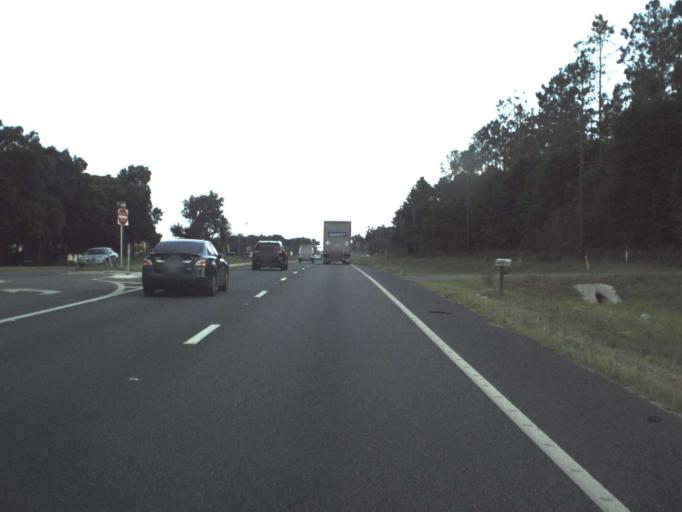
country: US
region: Florida
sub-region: Sumter County
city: Wildwood
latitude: 28.9132
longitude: -82.0371
